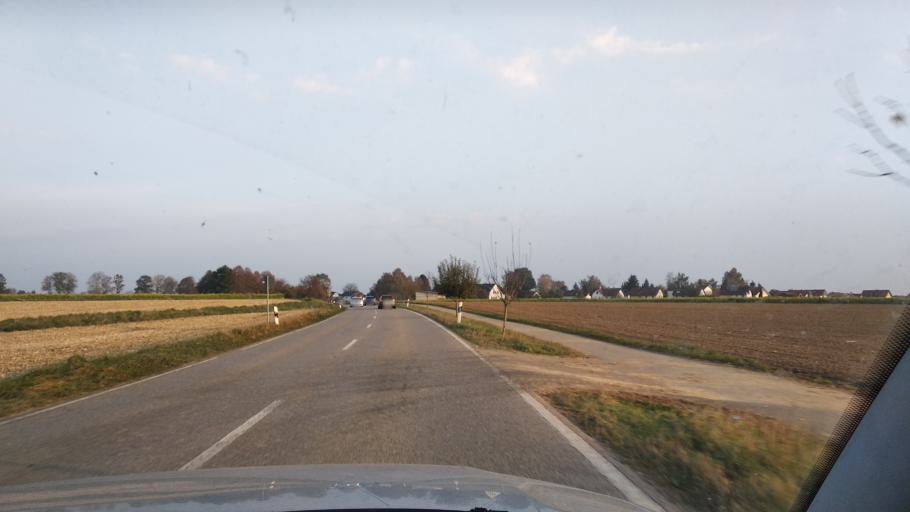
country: DE
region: Bavaria
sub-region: Upper Bavaria
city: Anzing
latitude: 48.1575
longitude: 11.8447
